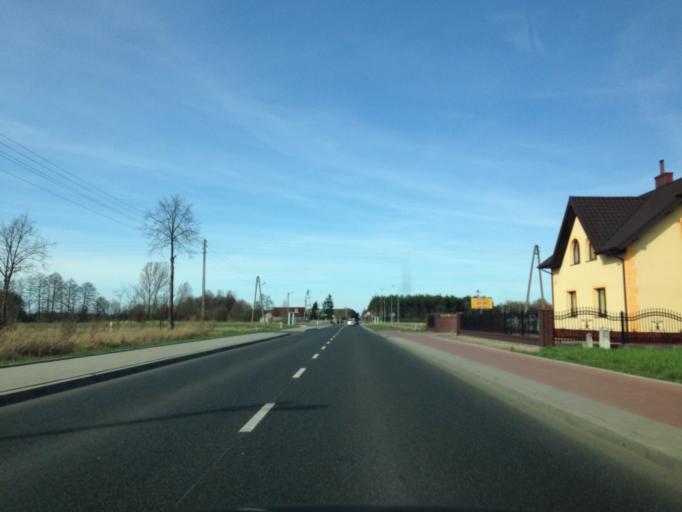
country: PL
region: Lodz Voivodeship
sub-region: Powiat poddebicki
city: Wartkowice
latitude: 51.9462
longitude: 18.9994
